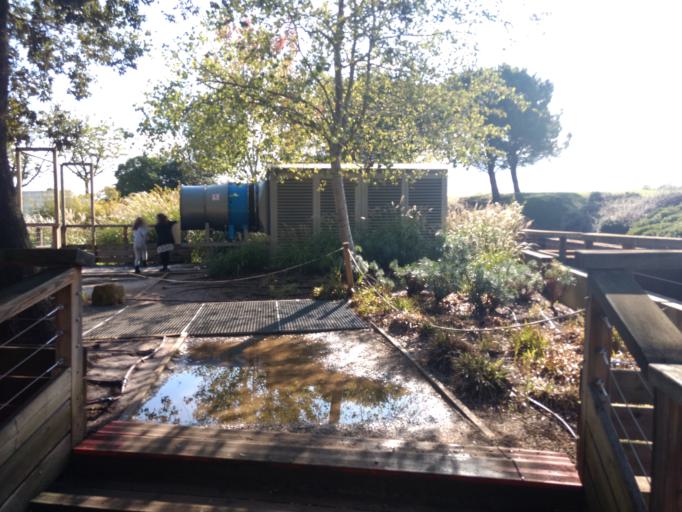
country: FR
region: Poitou-Charentes
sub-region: Departement de la Vienne
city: Chasseneuil-du-Poitou
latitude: 46.6674
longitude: 0.3660
